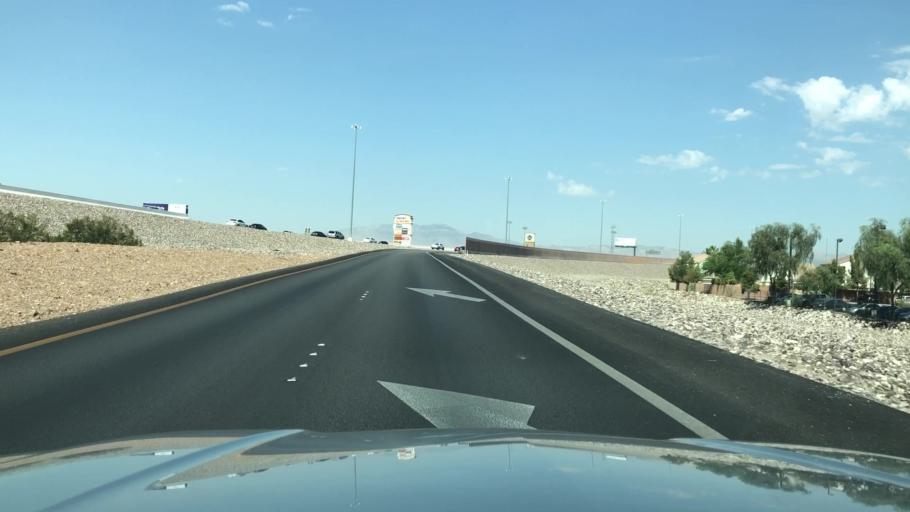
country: US
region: Nevada
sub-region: Clark County
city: Whitney
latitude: 36.0245
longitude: -115.1200
